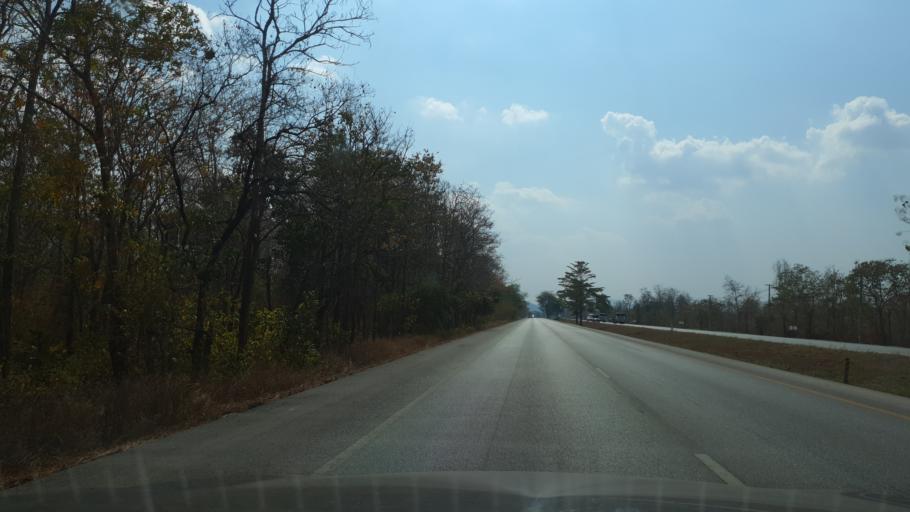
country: TH
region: Lampang
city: Mae Phrik
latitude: 17.4355
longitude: 99.1586
